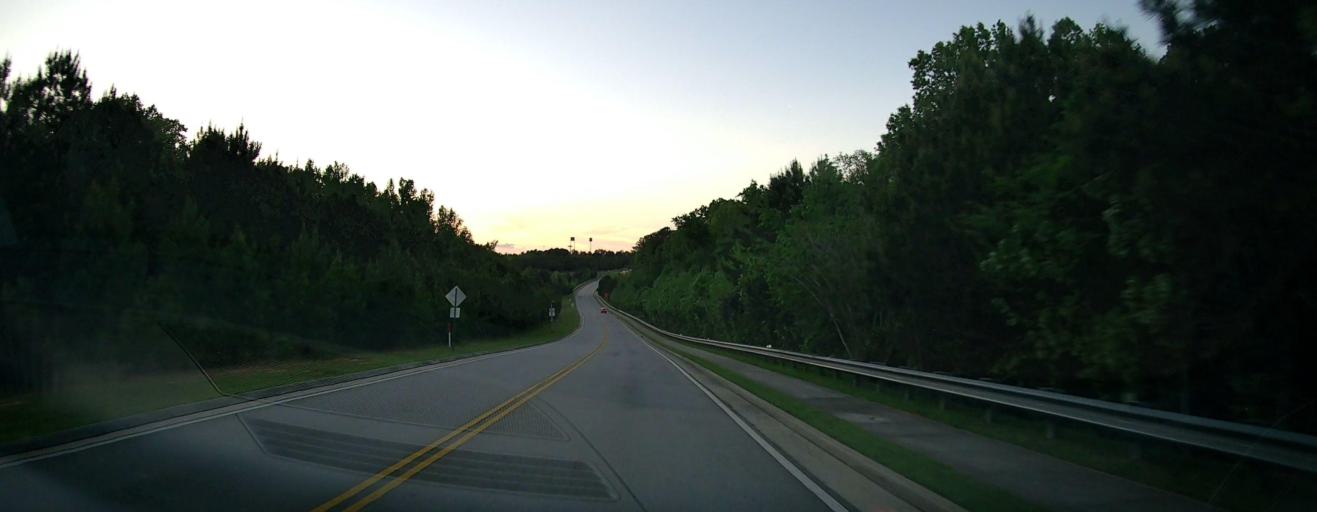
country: US
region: Georgia
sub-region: Henry County
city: Stockbridge
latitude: 33.4998
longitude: -84.2219
